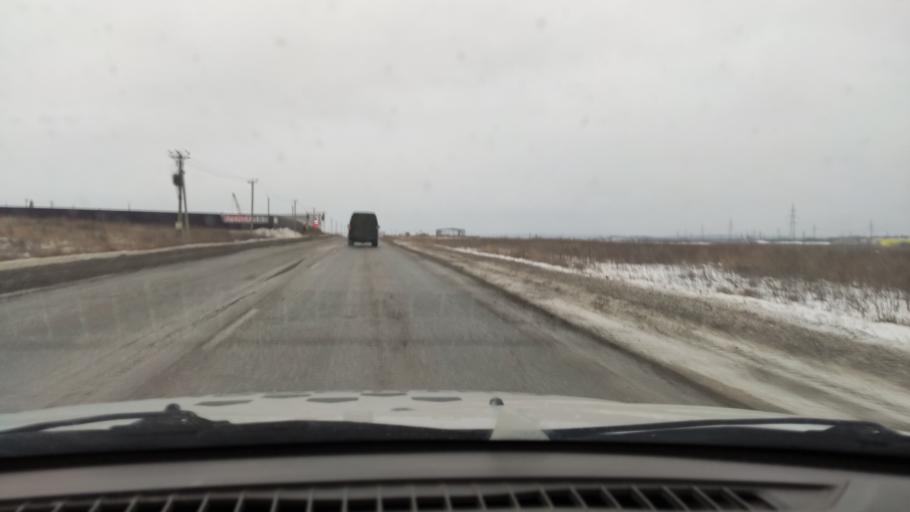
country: RU
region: Perm
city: Froly
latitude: 57.9177
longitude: 56.1836
